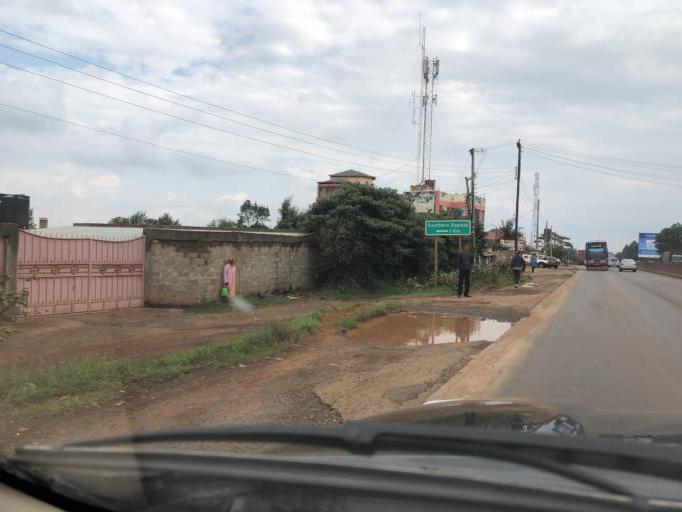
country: KE
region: Kiambu
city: Kikuyu
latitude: -1.2209
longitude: 36.6633
